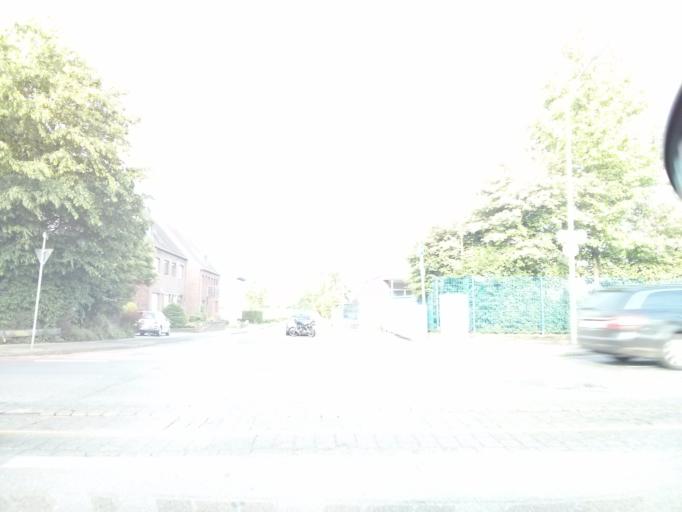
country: DE
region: North Rhine-Westphalia
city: Tonisvorst
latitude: 51.3669
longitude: 6.5157
